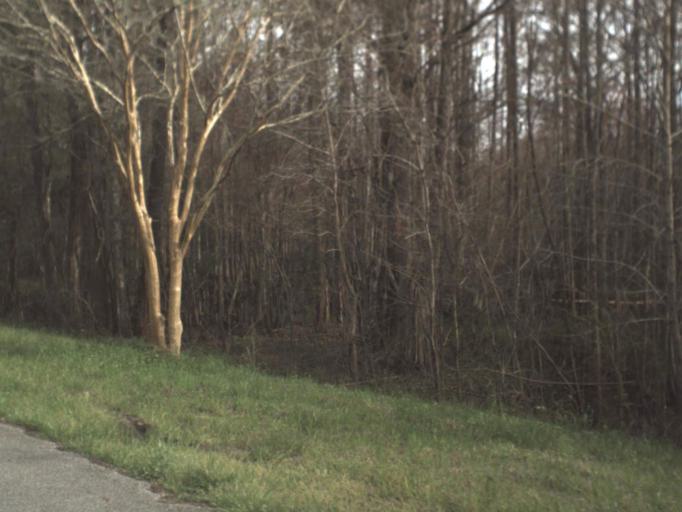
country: US
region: Florida
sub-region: Jefferson County
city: Monticello
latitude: 30.5287
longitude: -83.9765
